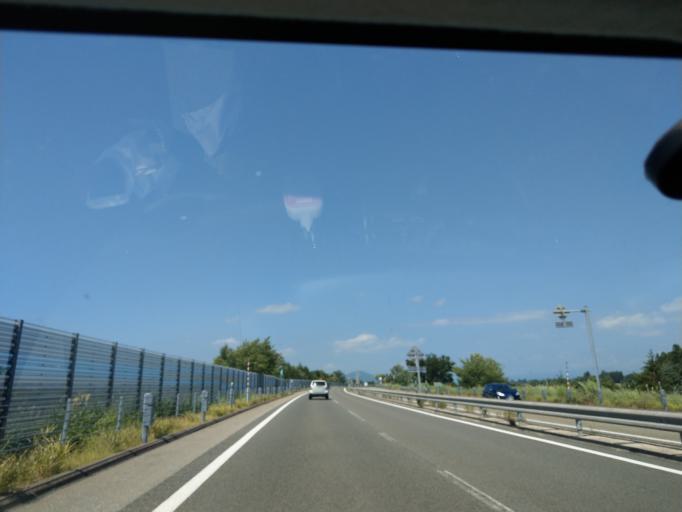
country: JP
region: Akita
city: Yokotemachi
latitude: 39.3597
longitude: 140.4898
